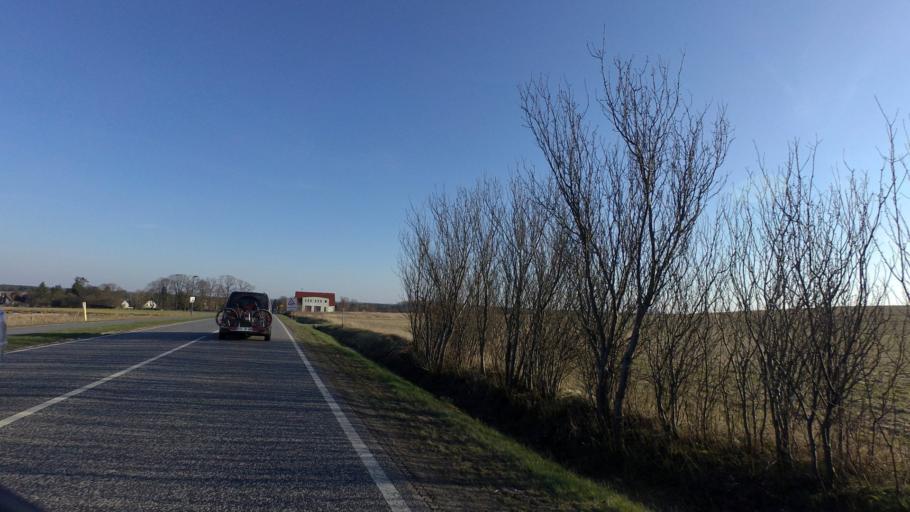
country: DE
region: Brandenburg
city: Britz
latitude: 52.8824
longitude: 13.8151
